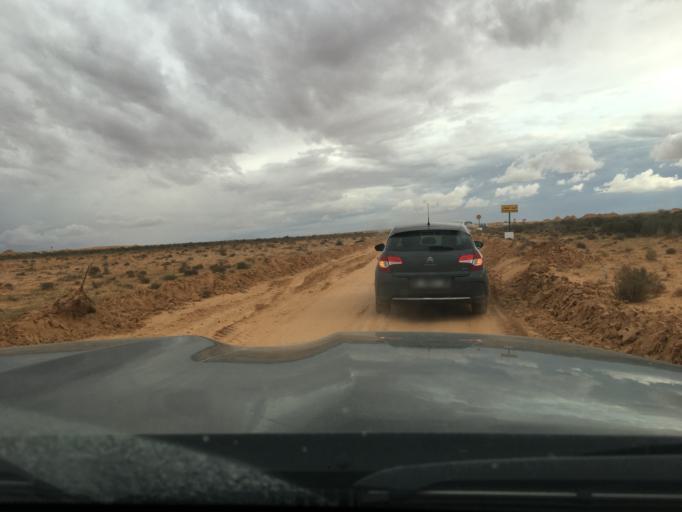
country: TN
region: Madanin
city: Medenine
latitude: 33.2614
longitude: 10.5727
